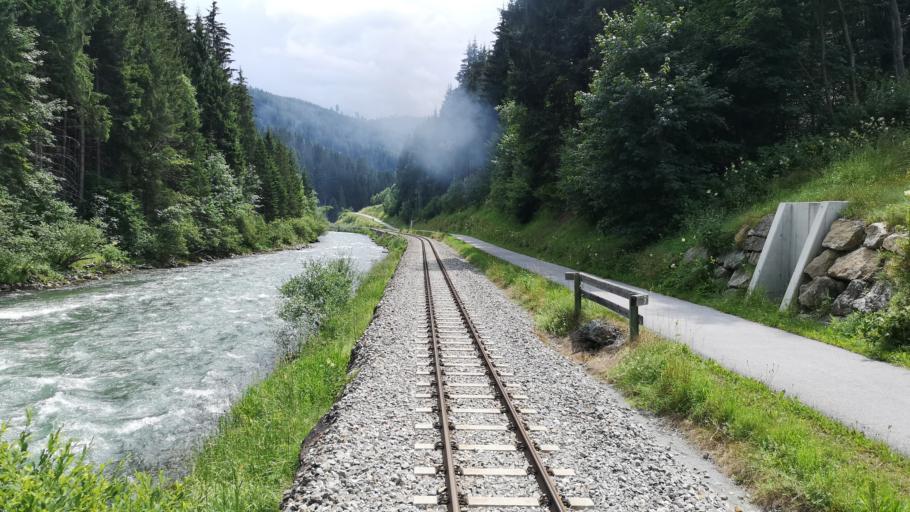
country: AT
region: Salzburg
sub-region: Politischer Bezirk Tamsweg
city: Tamsweg
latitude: 47.0990
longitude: 13.8212
